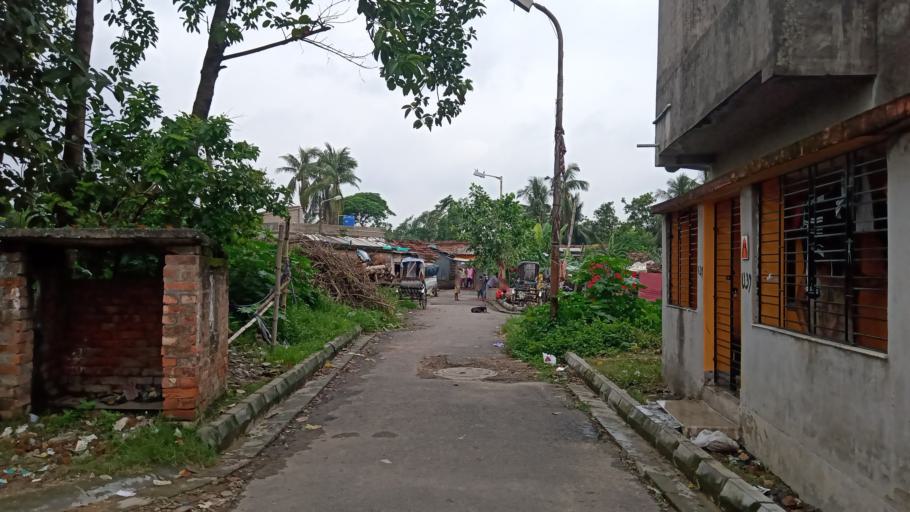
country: IN
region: West Bengal
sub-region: Kolkata
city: Kolkata
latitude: 22.4666
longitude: 88.3880
